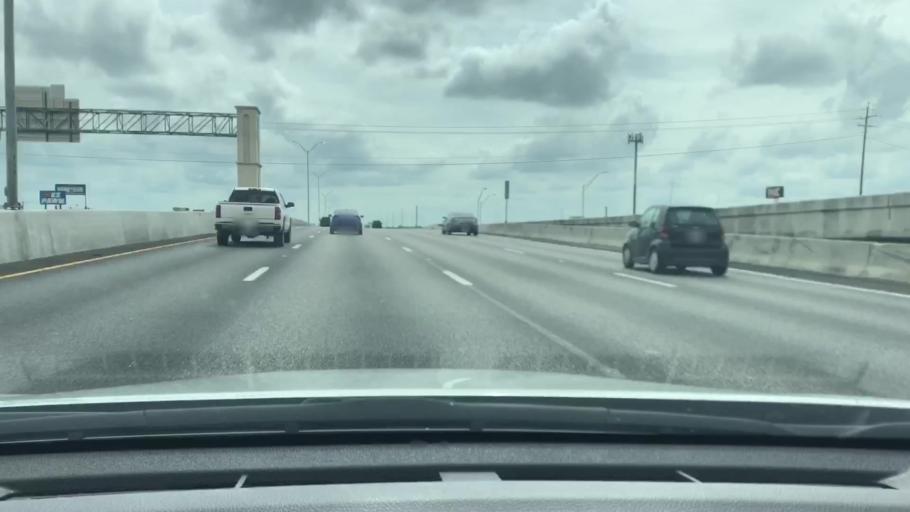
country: US
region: Texas
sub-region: Bexar County
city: Windcrest
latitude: 29.5118
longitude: -98.3980
